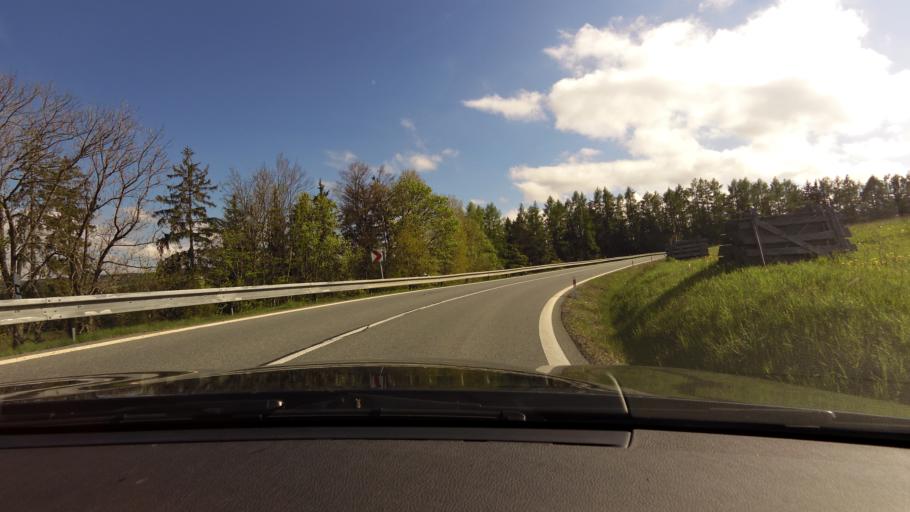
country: CZ
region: Plzensky
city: Strazov
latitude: 49.2495
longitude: 13.3070
